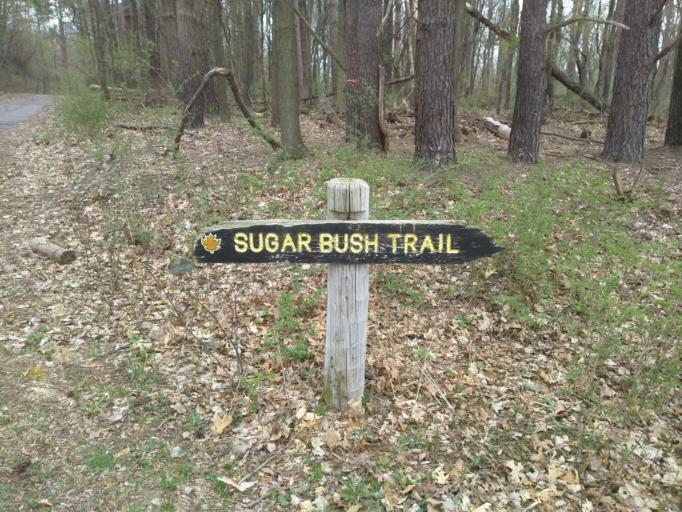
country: US
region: Michigan
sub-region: Ingham County
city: Lansing
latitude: 42.7096
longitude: -84.5183
